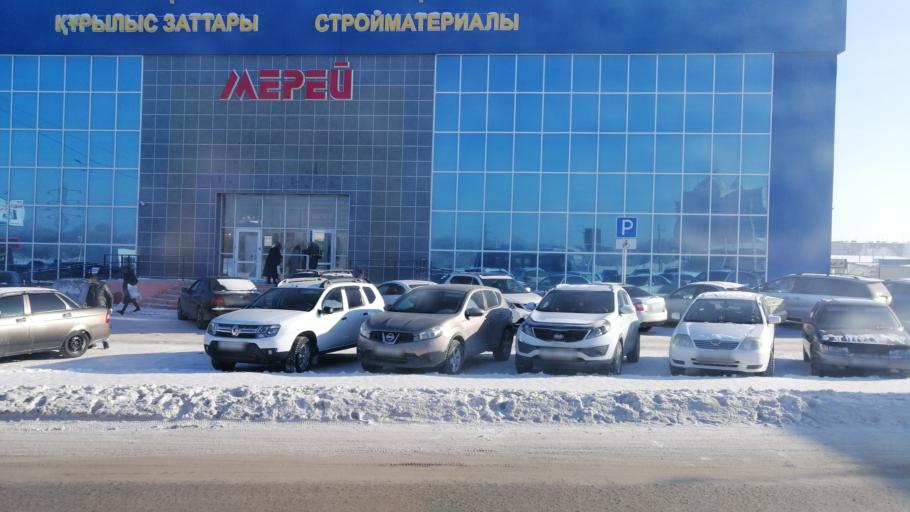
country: KZ
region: Aqtoebe
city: Aqtobe
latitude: 50.2950
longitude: 57.1978
